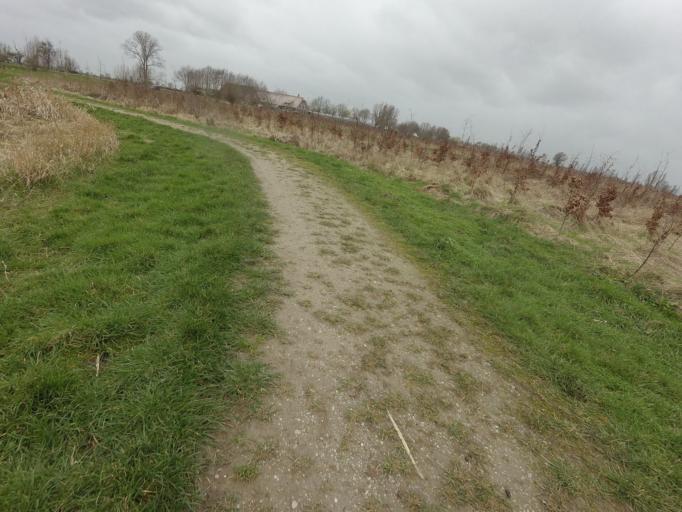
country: NL
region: Utrecht
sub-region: Gemeente IJsselstein
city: IJsselstein
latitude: 52.0436
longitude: 5.0305
